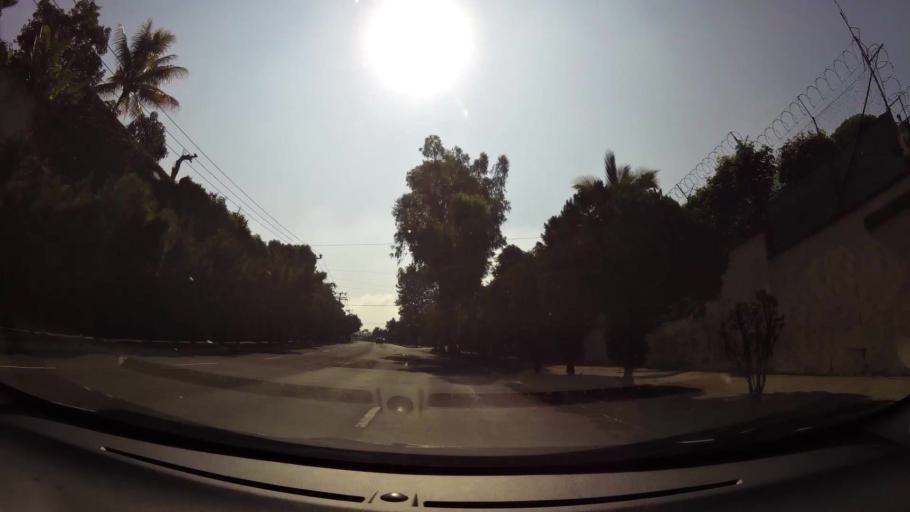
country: SV
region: La Libertad
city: Antiguo Cuscatlan
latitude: 13.6701
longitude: -89.2376
